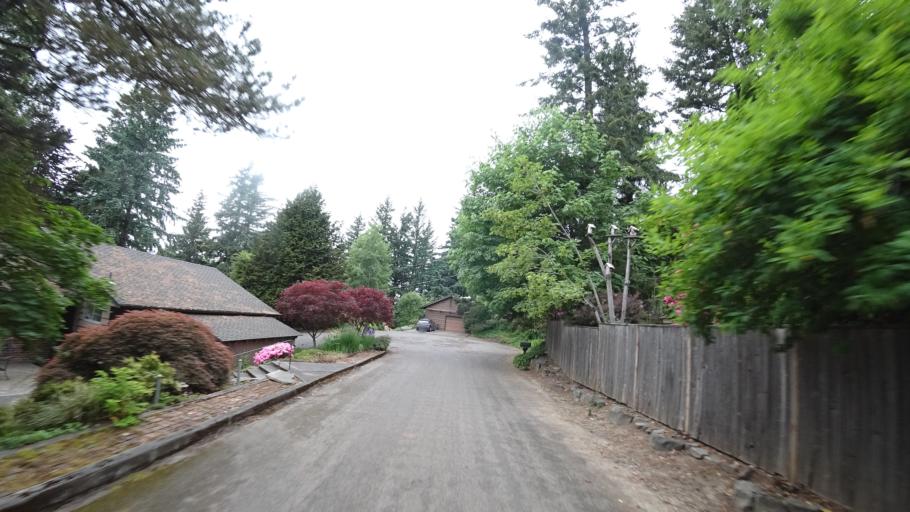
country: US
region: Oregon
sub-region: Multnomah County
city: Portland
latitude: 45.4858
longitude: -122.6937
